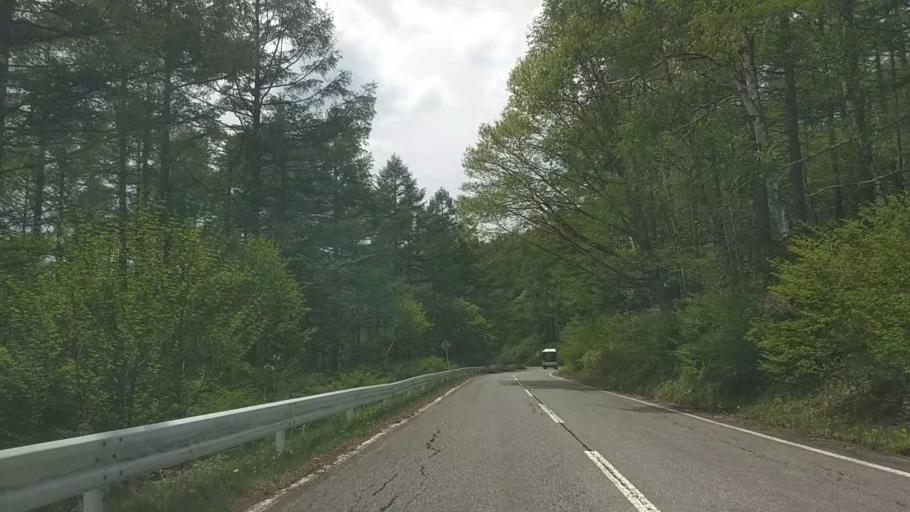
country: JP
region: Nagano
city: Saku
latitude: 36.0902
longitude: 138.3901
